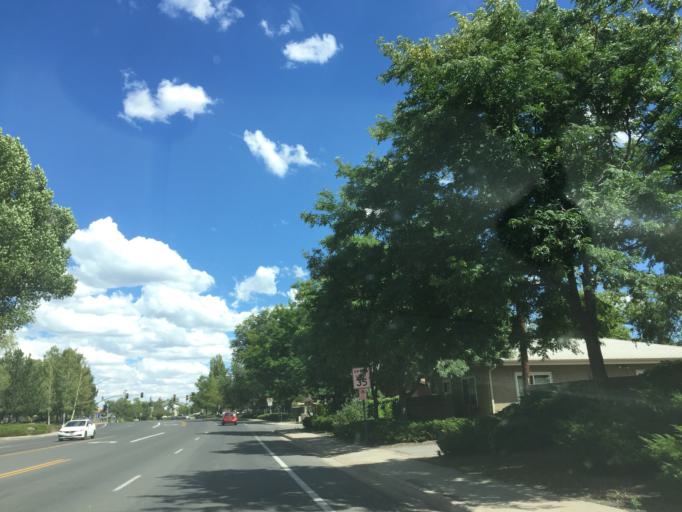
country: US
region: Arizona
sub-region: Coconino County
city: Flagstaff
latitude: 35.1941
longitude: -111.6517
